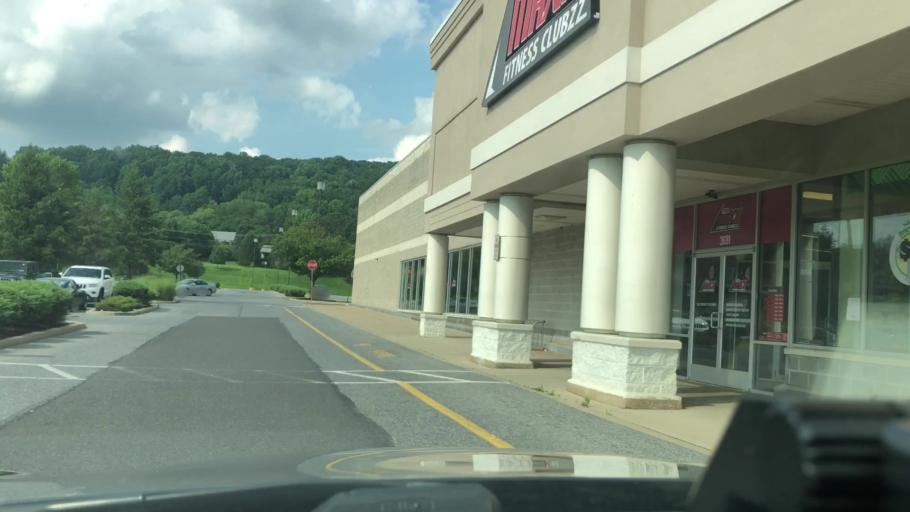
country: US
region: Pennsylvania
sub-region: Lehigh County
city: Fountain Hill
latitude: 40.5856
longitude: -75.3859
